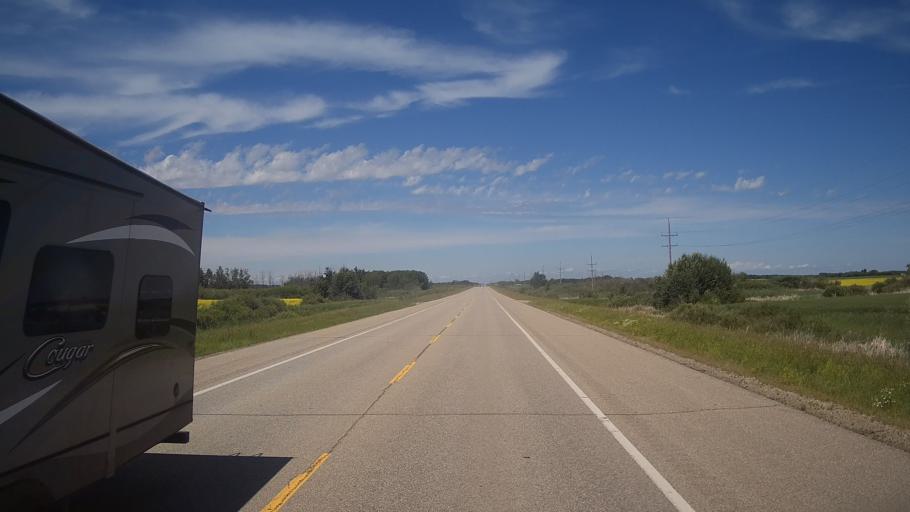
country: CA
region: Saskatchewan
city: Langenburg
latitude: 50.6412
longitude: -101.2760
